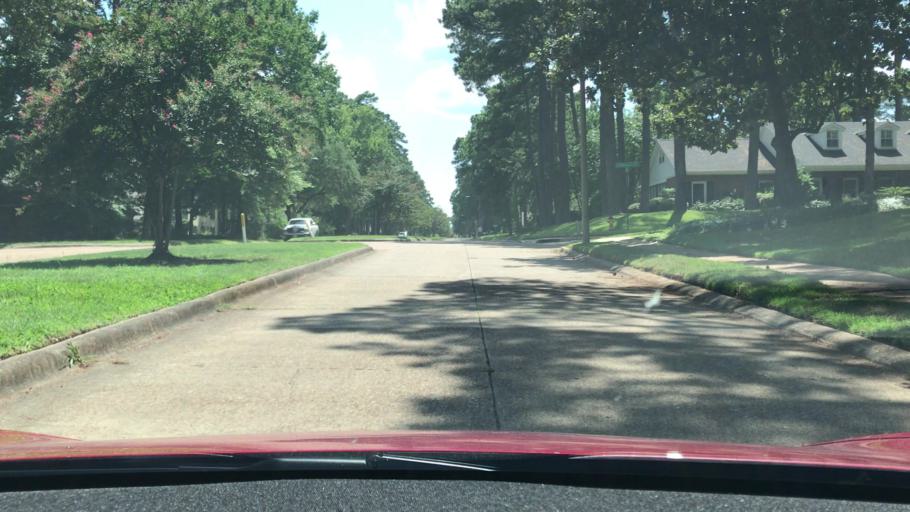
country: US
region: Louisiana
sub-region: Bossier Parish
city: Bossier City
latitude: 32.4303
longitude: -93.7325
